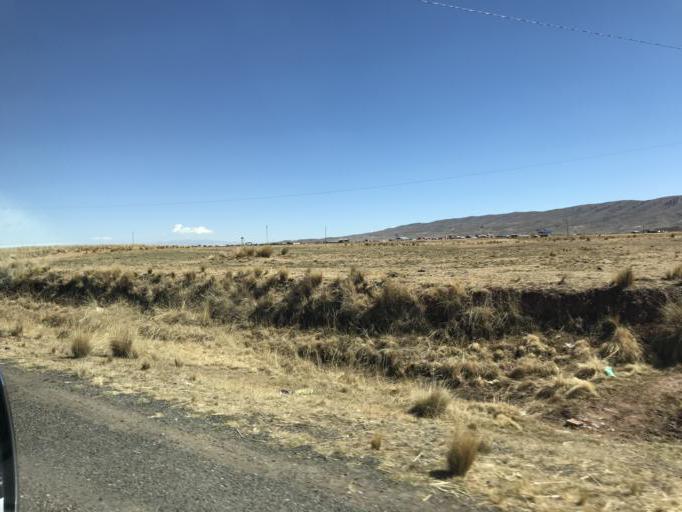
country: BO
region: La Paz
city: Tiahuanaco
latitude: -16.5703
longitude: -68.6682
